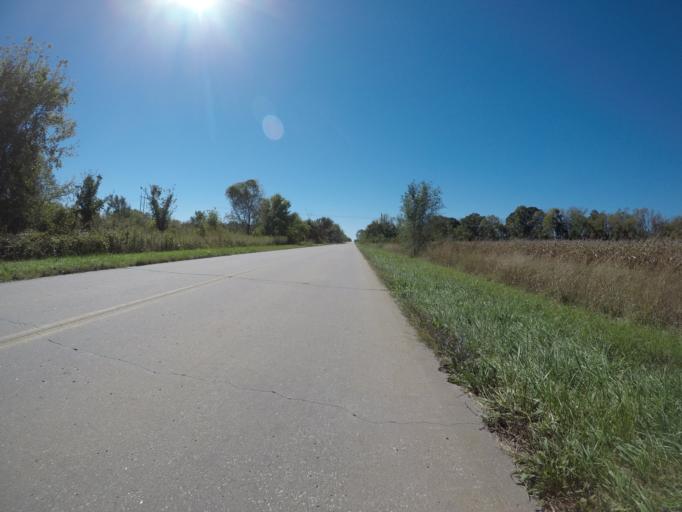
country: US
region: Kansas
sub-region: Wyandotte County
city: Bonner Springs
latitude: 39.0330
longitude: -94.8960
